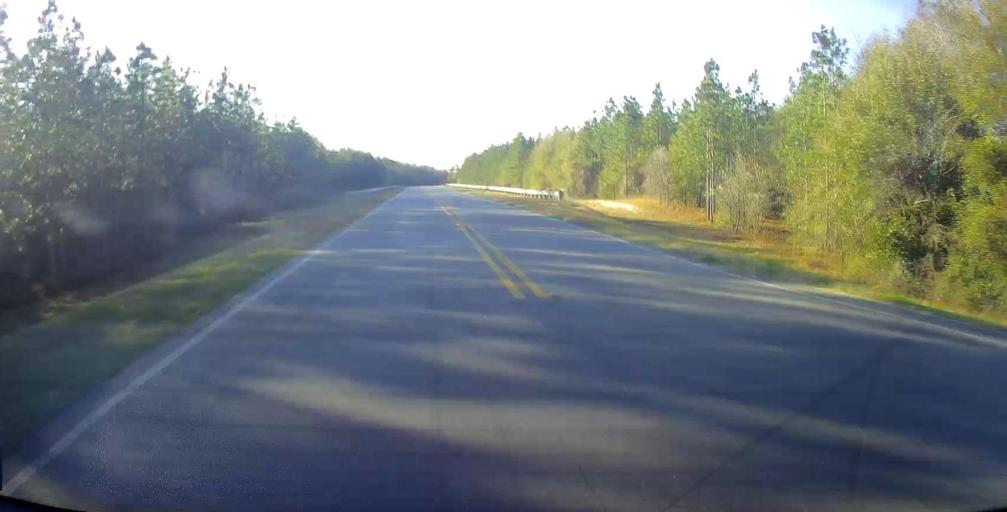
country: US
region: Georgia
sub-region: Pulaski County
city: Hawkinsville
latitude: 32.2757
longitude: -83.4462
